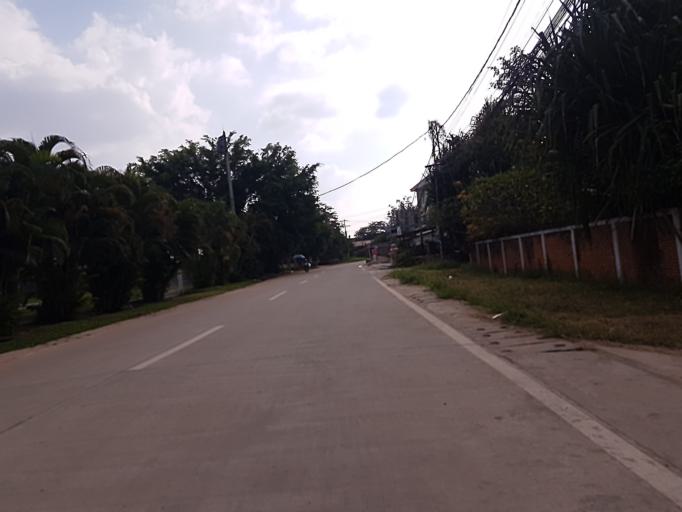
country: LA
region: Vientiane
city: Vientiane
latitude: 17.9327
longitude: 102.6200
